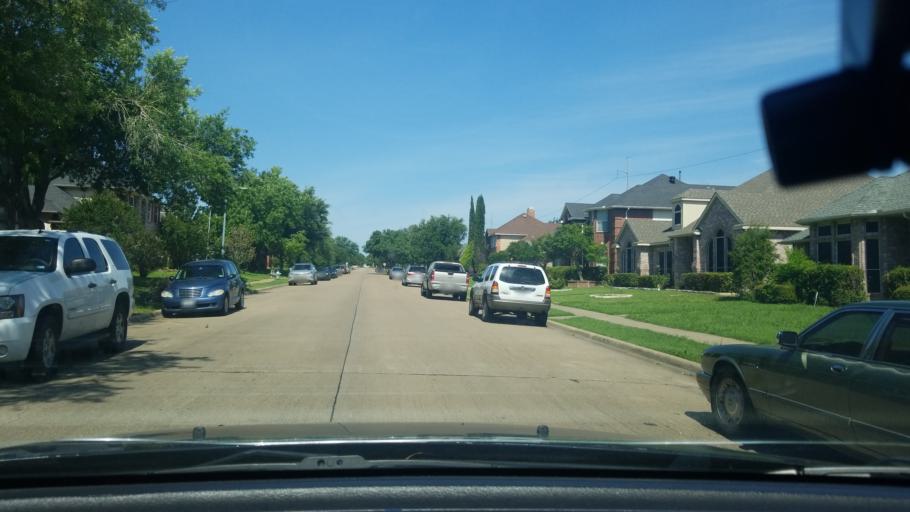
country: US
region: Texas
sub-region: Dallas County
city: Mesquite
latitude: 32.7750
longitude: -96.5871
